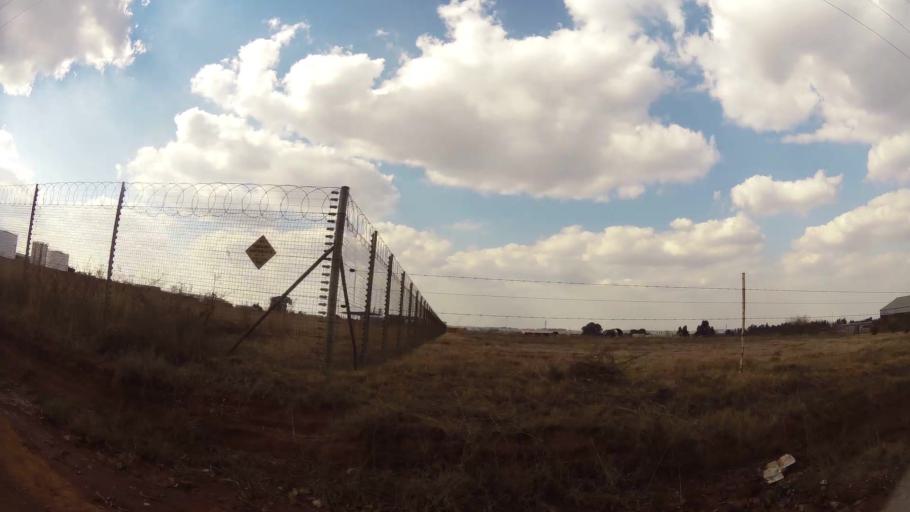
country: ZA
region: Mpumalanga
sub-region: Nkangala District Municipality
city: Delmas
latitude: -26.1313
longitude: 28.6779
